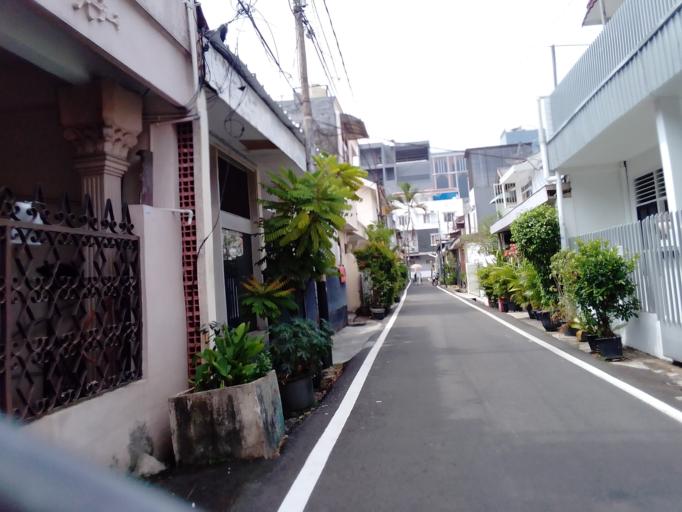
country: ID
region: Jakarta Raya
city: Jakarta
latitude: -6.1748
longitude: 106.8103
